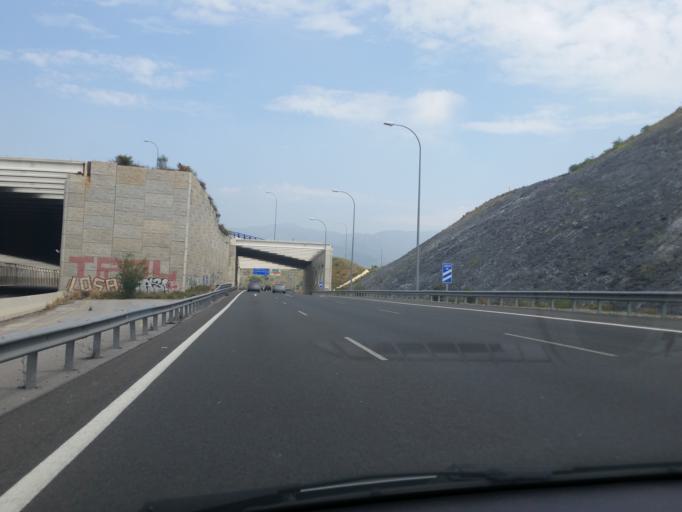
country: ES
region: Andalusia
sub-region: Provincia de Malaga
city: Malaga
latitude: 36.7430
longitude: -4.4443
